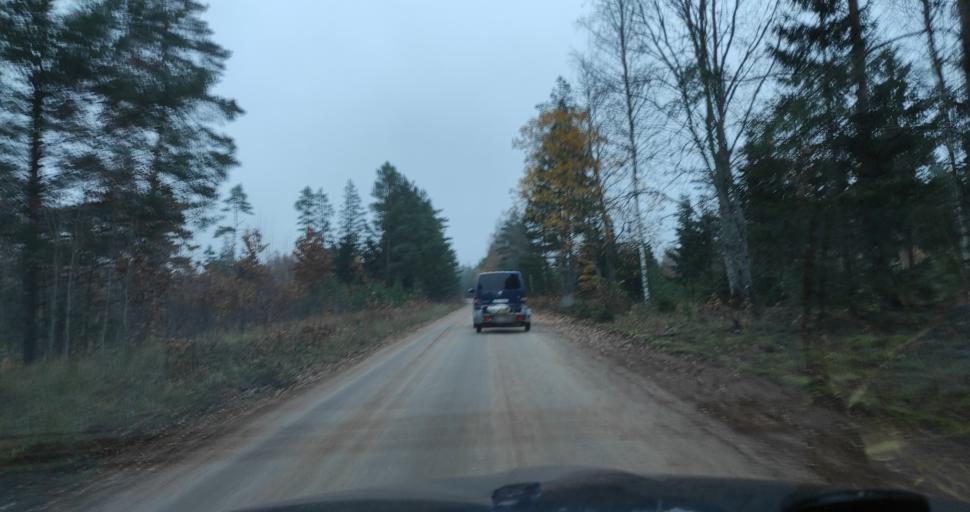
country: LV
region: Pavilostas
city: Pavilosta
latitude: 56.7570
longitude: 21.2681
